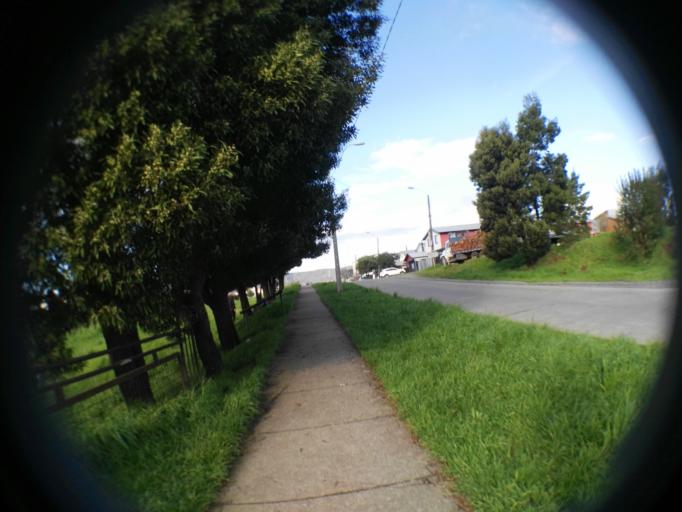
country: CL
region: Los Lagos
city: Las Animas
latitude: -39.8342
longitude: -73.2265
